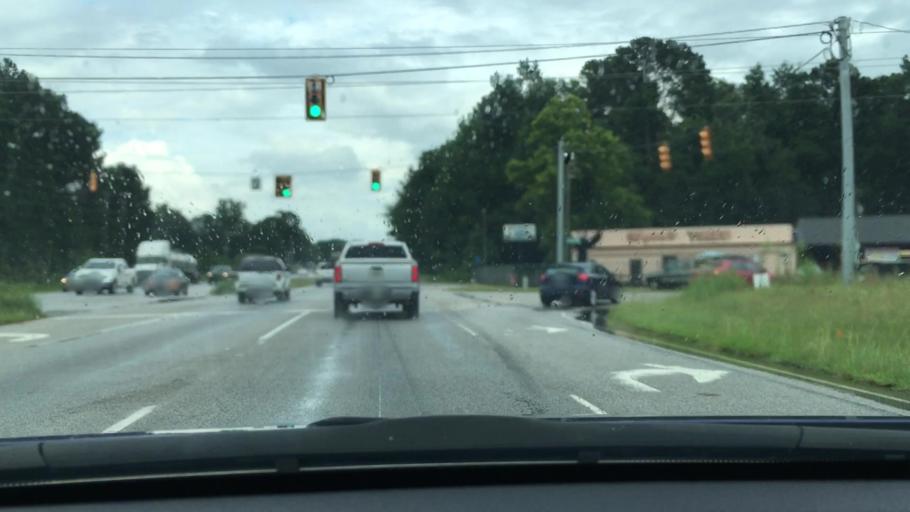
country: US
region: South Carolina
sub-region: Sumter County
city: Cherryvale
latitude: 33.9627
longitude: -80.4212
